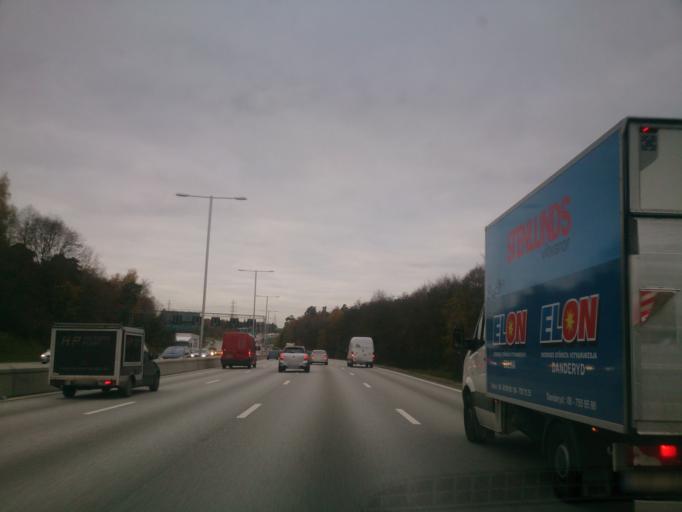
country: SE
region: Stockholm
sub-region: Solna Kommun
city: Rasunda
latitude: 59.3892
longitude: 17.9991
